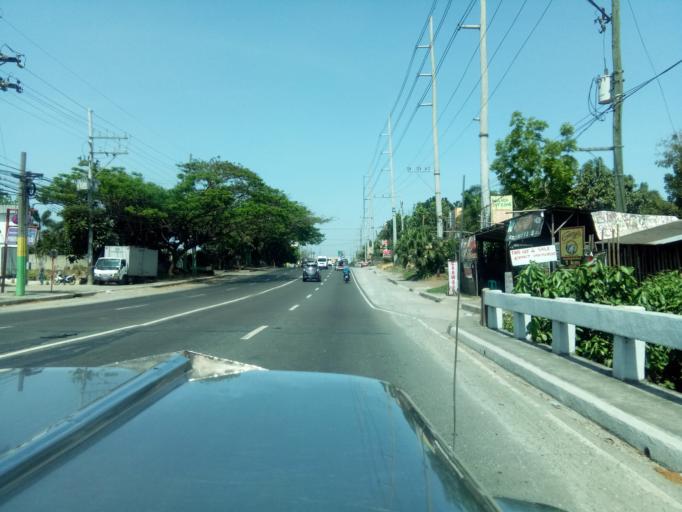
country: PH
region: Calabarzon
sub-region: Province of Cavite
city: Dasmarinas
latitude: 14.2974
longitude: 120.9472
